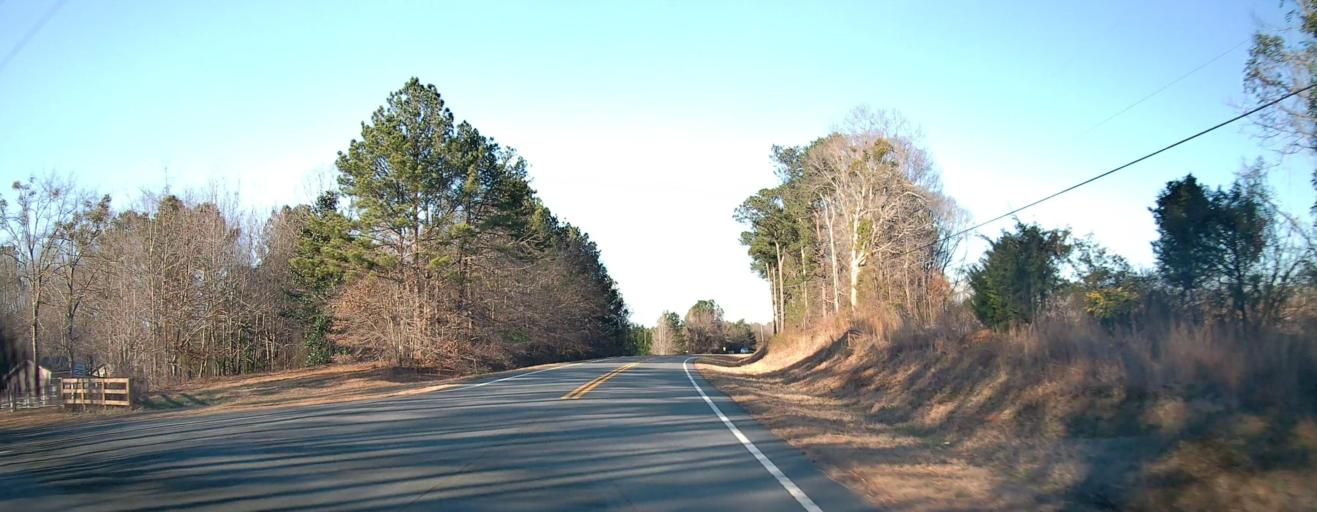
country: US
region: Georgia
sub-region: Meriwether County
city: Manchester
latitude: 32.9022
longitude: -84.6807
